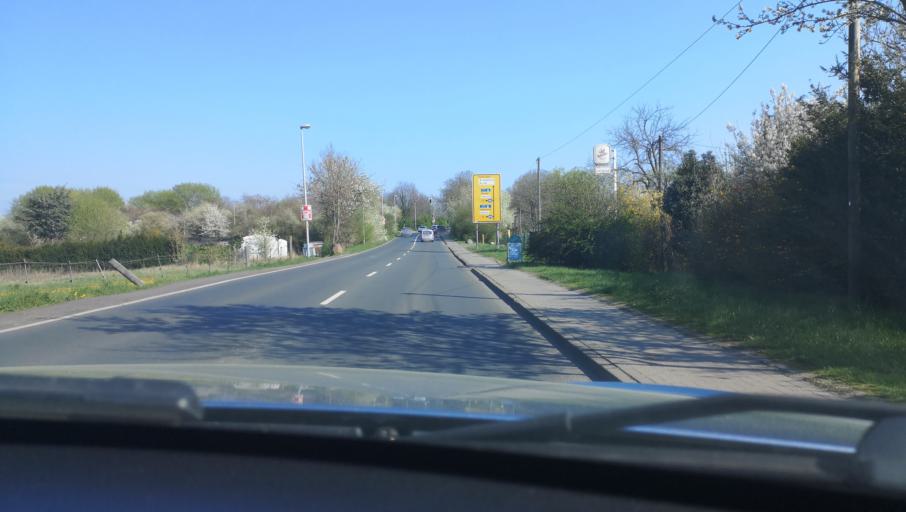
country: DE
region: Saxony-Anhalt
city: Diesdorf
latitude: 52.0831
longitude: 11.5858
